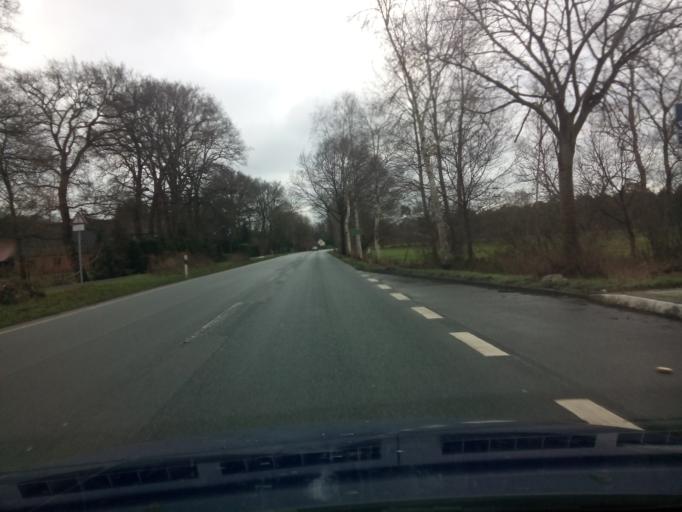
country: DE
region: Lower Saxony
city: Worpswede
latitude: 53.2469
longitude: 8.9576
